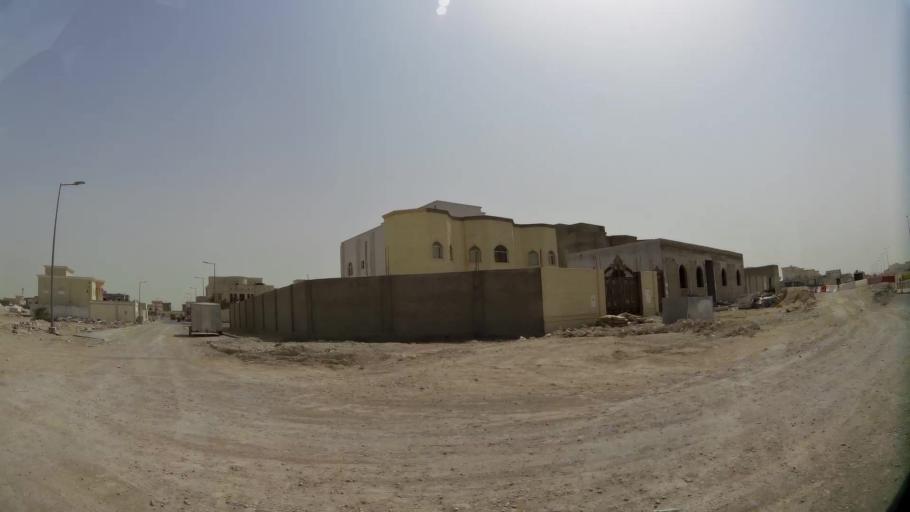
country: QA
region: Baladiyat ar Rayyan
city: Ar Rayyan
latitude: 25.2618
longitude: 51.3683
